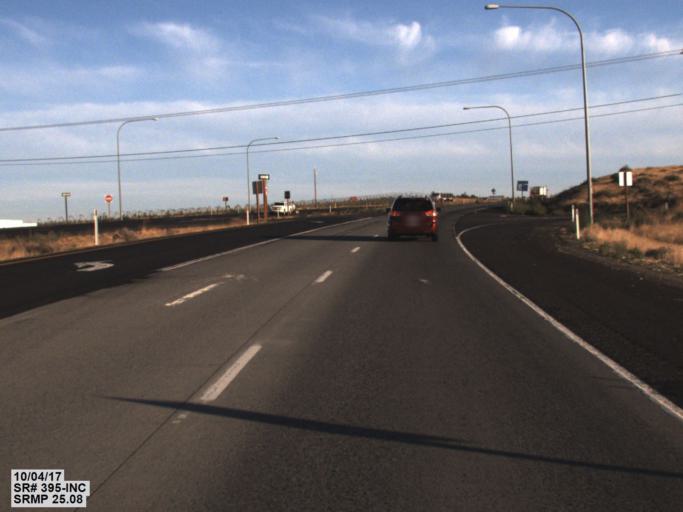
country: US
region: Washington
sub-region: Franklin County
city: Pasco
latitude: 46.2847
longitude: -119.0933
